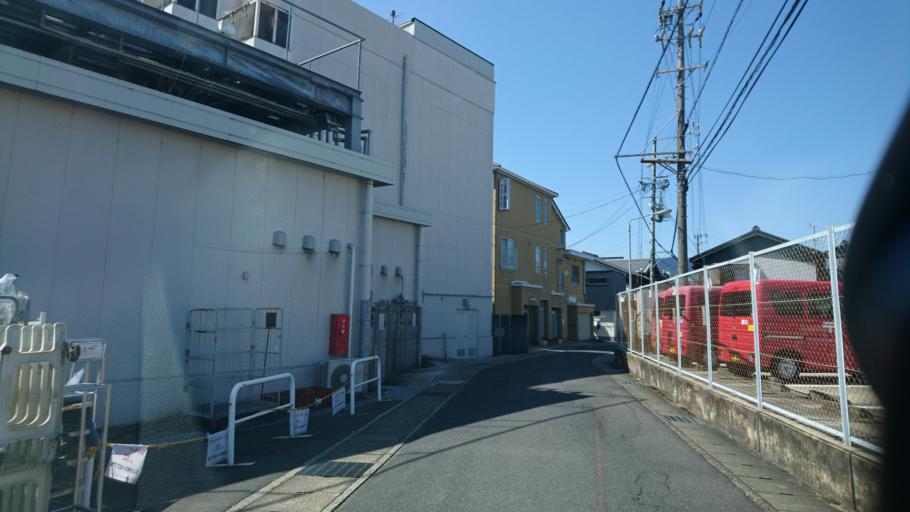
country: JP
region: Gifu
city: Nakatsugawa
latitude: 35.4525
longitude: 137.4116
